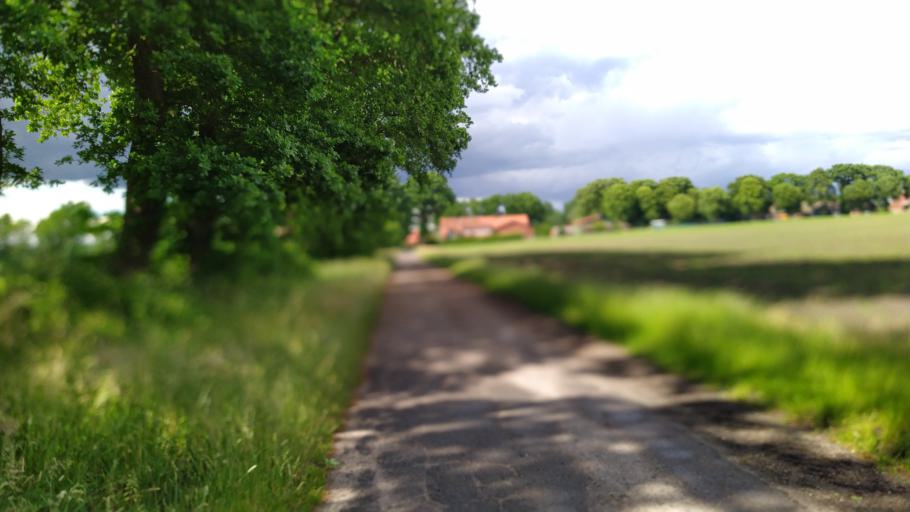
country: DE
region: Lower Saxony
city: Deinstedt
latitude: 53.4411
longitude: 9.2590
